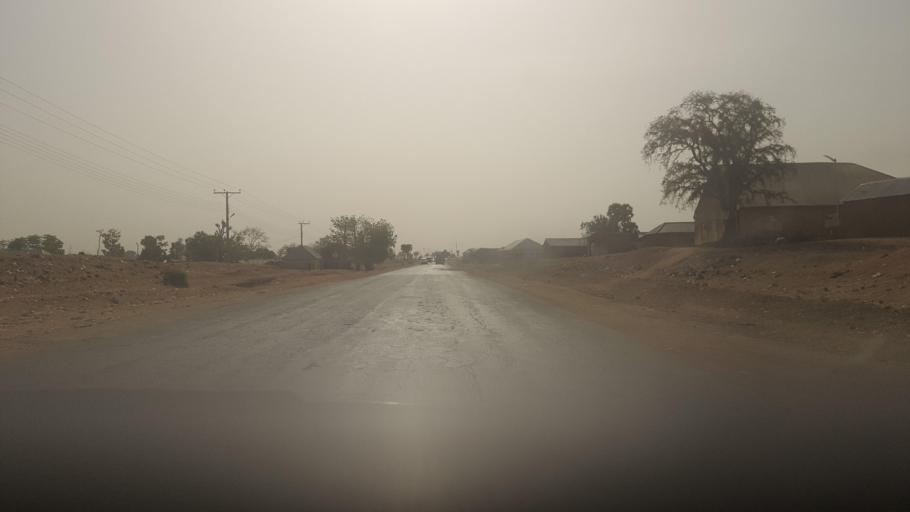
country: NG
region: Bauchi
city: Bauchi
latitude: 10.2613
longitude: 9.9943
